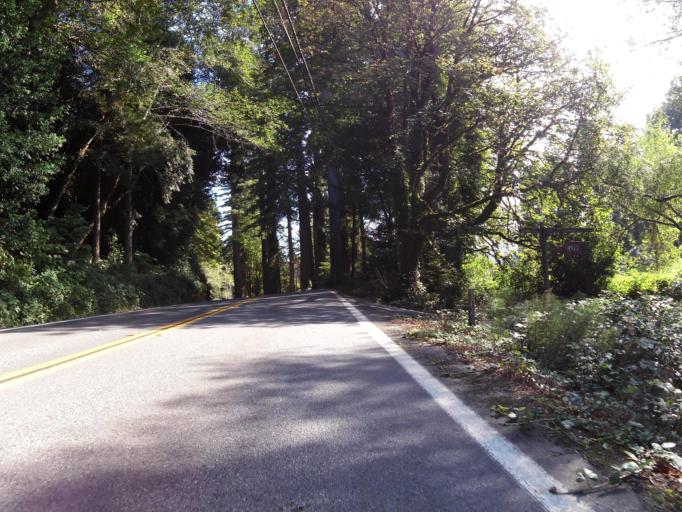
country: US
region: California
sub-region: Del Norte County
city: Bertsch-Oceanview
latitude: 41.8432
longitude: -124.1137
